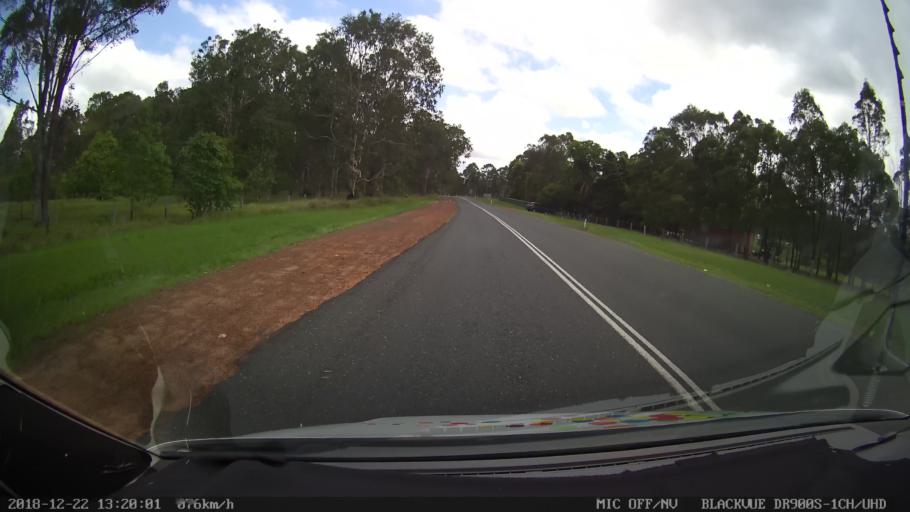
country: AU
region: New South Wales
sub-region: Clarence Valley
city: South Grafton
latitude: -29.7620
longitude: 152.9297
